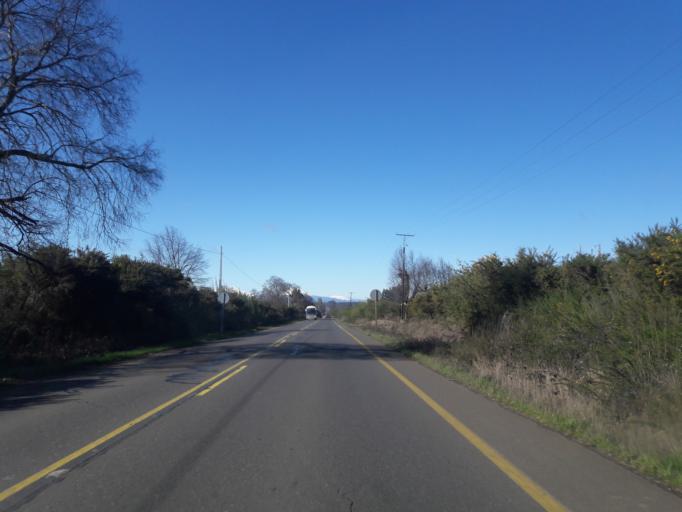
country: CL
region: Araucania
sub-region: Provincia de Malleco
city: Victoria
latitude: -38.2561
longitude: -72.2706
